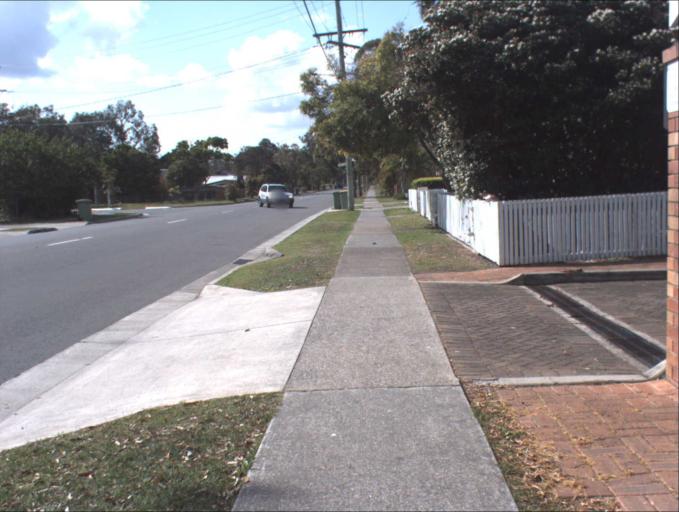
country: AU
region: Queensland
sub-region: Logan
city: Waterford West
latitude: -27.6747
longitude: 153.1313
